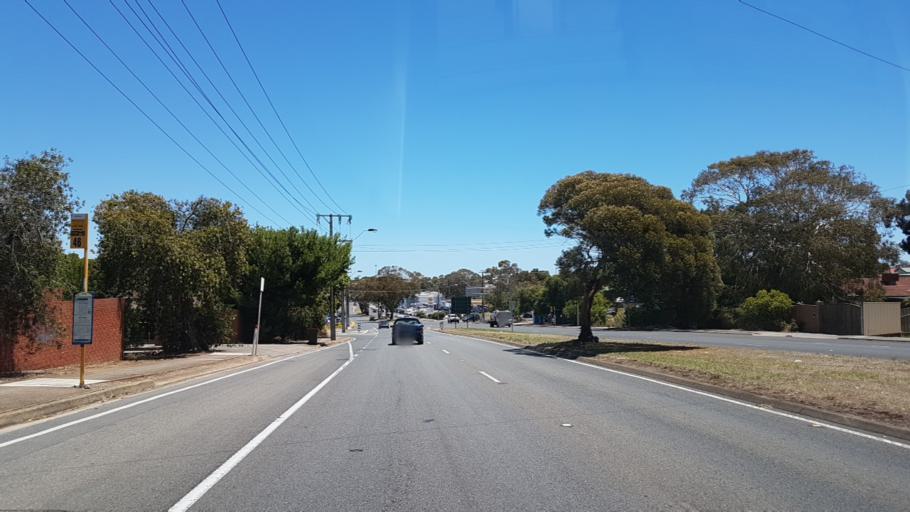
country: AU
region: South Australia
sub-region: Onkaparinga
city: Reynella
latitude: -35.0982
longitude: 138.5342
